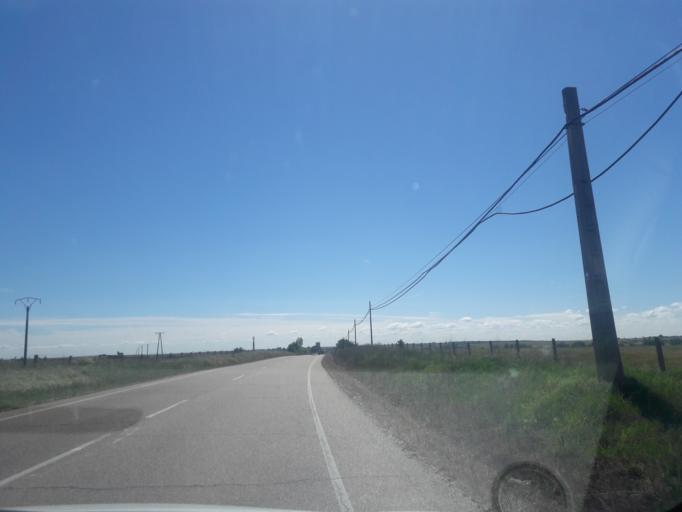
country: ES
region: Castille and Leon
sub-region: Provincia de Salamanca
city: Vitigudino
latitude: 41.0104
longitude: -6.4514
